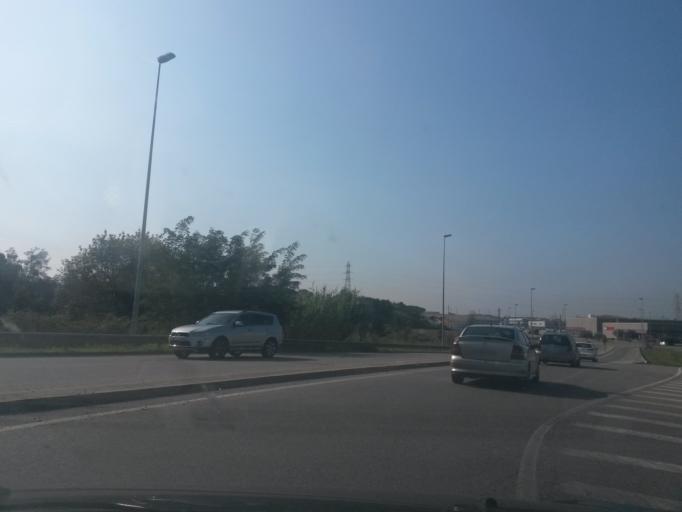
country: ES
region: Catalonia
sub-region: Provincia de Girona
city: Fornells de la Selva
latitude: 41.9423
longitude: 2.8050
